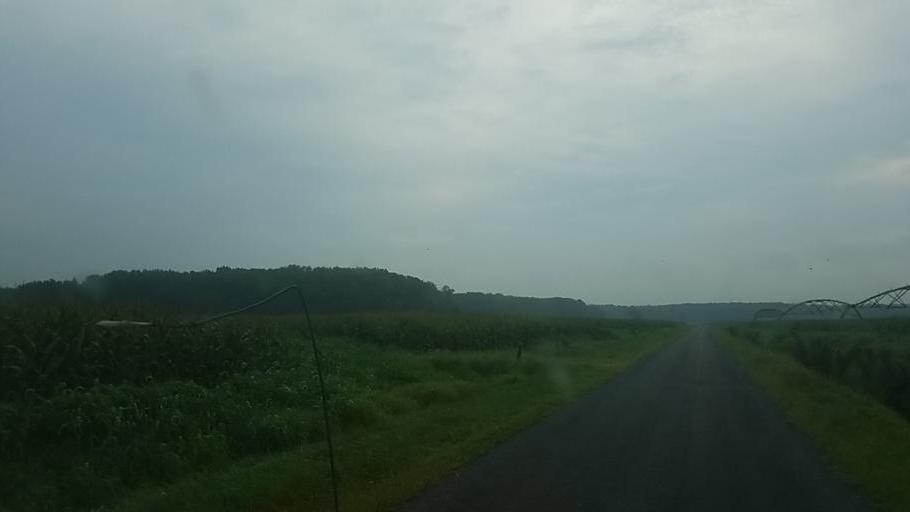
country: US
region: Delaware
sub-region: Sussex County
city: Selbyville
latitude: 38.4489
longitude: -75.2847
